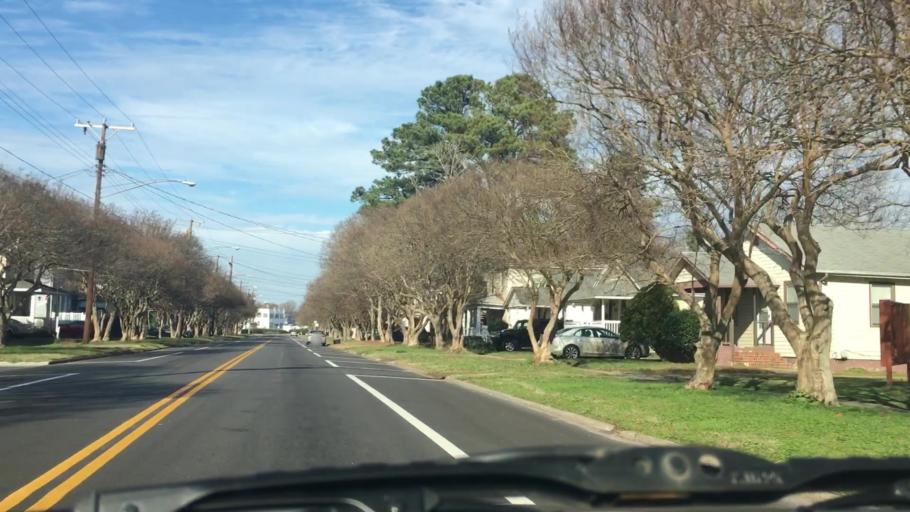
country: US
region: Virginia
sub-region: City of Norfolk
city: Norfolk
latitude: 36.8718
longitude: -76.2526
